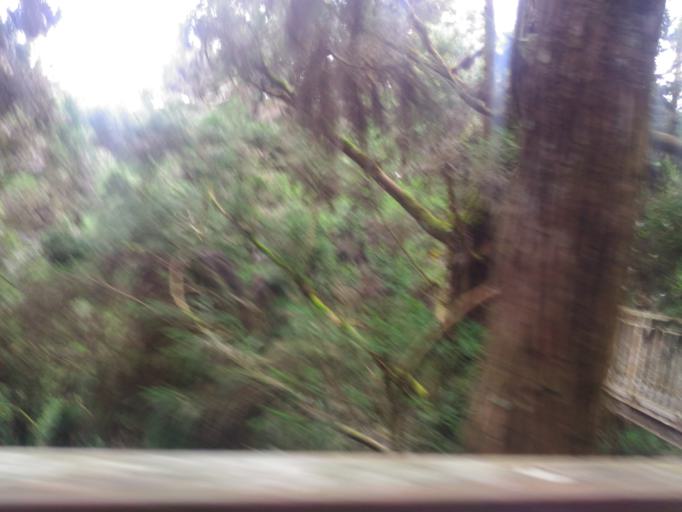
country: TW
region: Taiwan
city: Lugu
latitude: 23.6638
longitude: 120.7935
